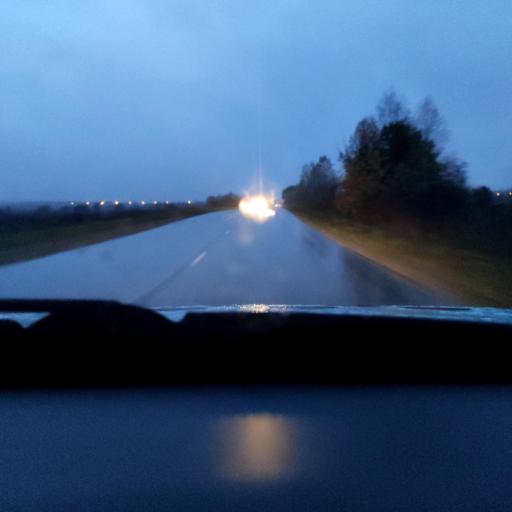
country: RU
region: Perm
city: Kondratovo
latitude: 57.9978
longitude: 56.0804
